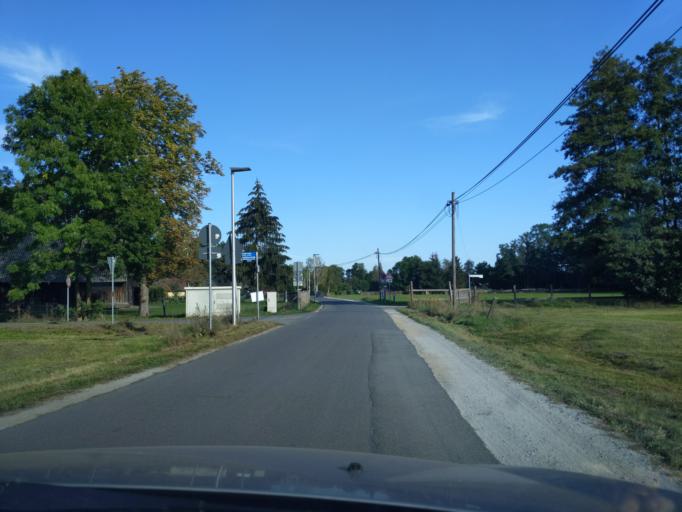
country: DE
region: Brandenburg
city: Burg
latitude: 51.8611
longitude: 14.0977
